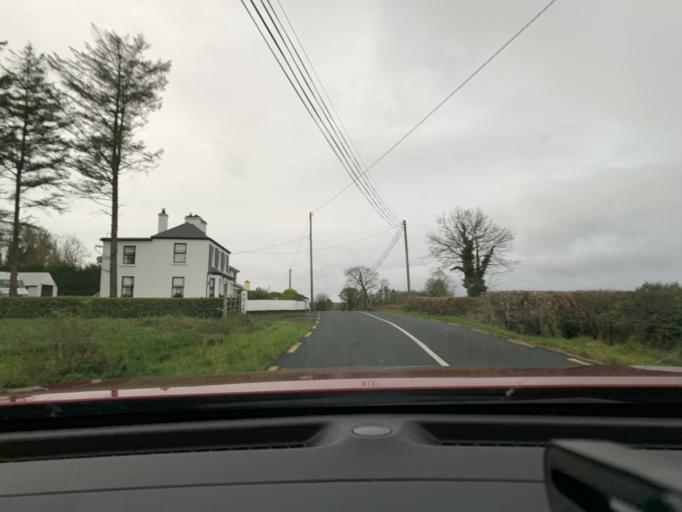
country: IE
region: Connaught
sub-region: Sligo
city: Ballymote
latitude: 54.0131
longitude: -8.5233
